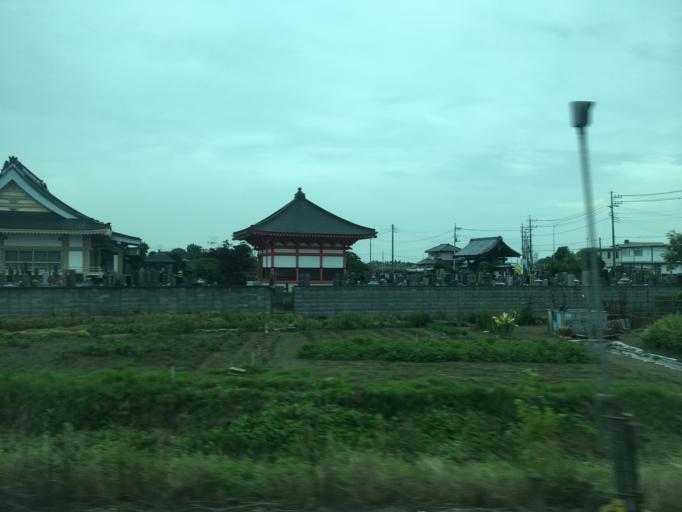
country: JP
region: Saitama
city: Kukichuo
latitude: 36.1004
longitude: 139.6787
